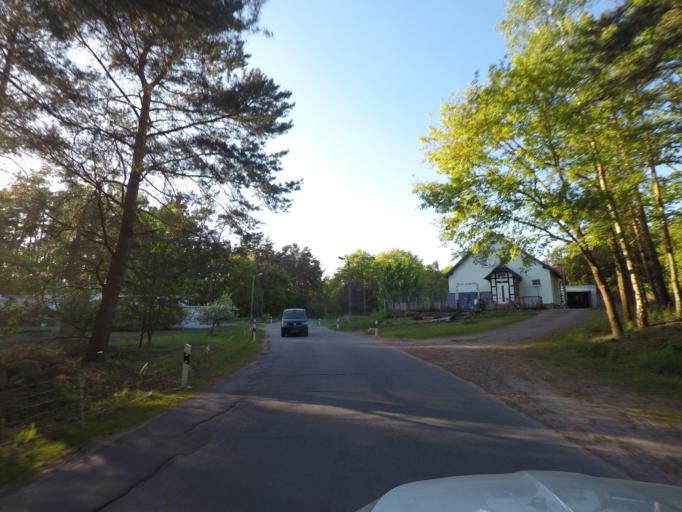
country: DE
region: Brandenburg
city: Bad Freienwalde
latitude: 52.8278
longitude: 14.0084
